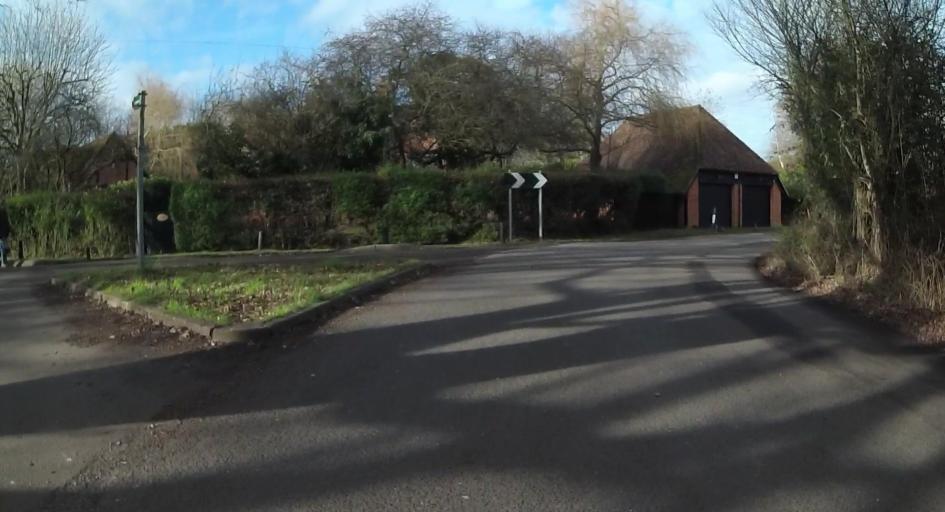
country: GB
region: England
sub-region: Wokingham
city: Barkham
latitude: 51.3972
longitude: -0.8537
